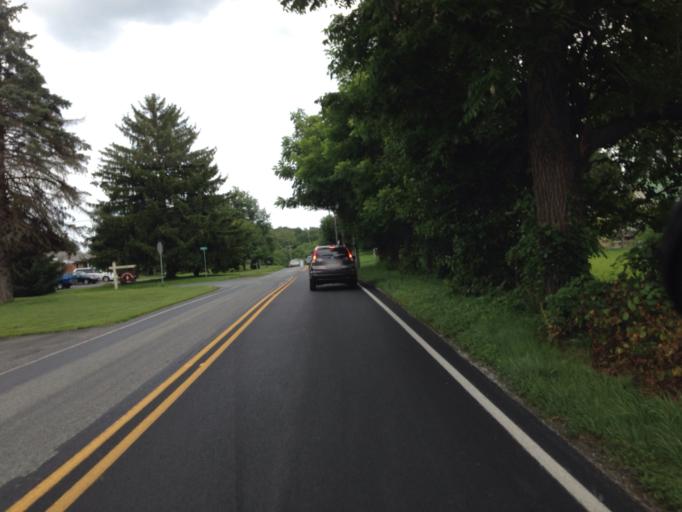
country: US
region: Pennsylvania
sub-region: Chester County
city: West Grove
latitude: 39.7798
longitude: -75.8719
